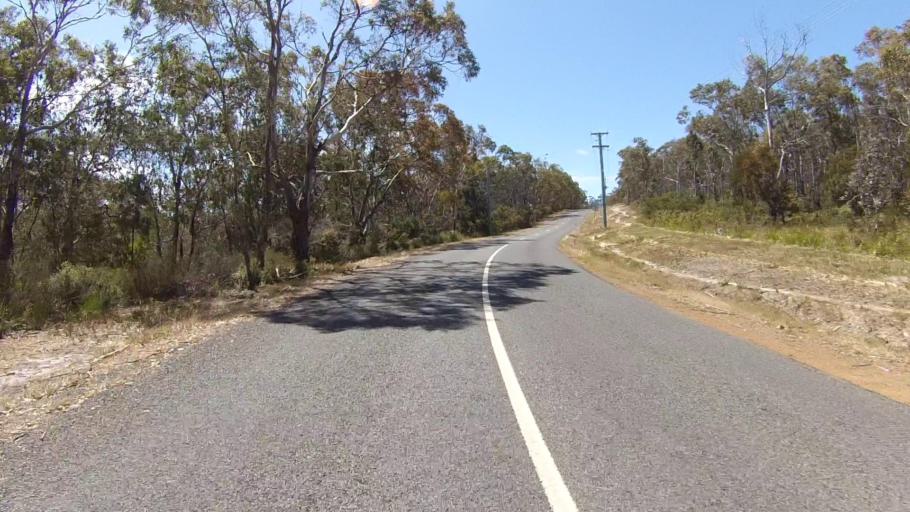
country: AU
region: Tasmania
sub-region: Clarence
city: Sandford
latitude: -43.0220
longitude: 147.4796
